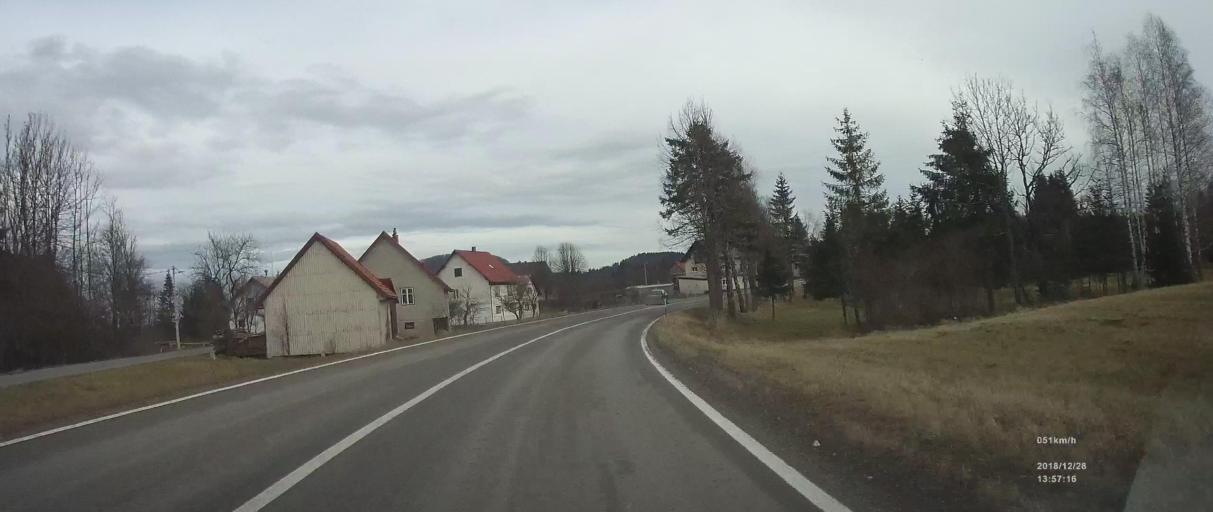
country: HR
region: Primorsko-Goranska
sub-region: Grad Delnice
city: Delnice
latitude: 45.3946
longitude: 14.8854
